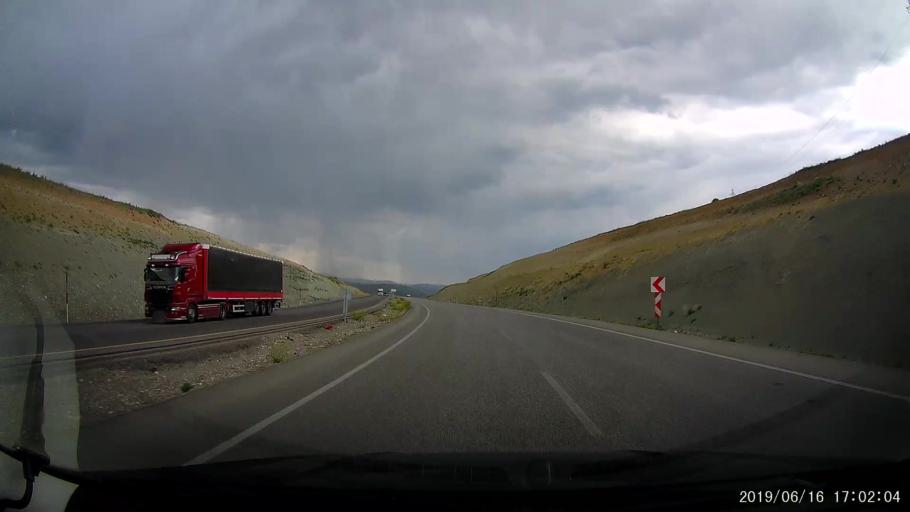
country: TR
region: Erzurum
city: Askale
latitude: 39.9433
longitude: 40.7619
